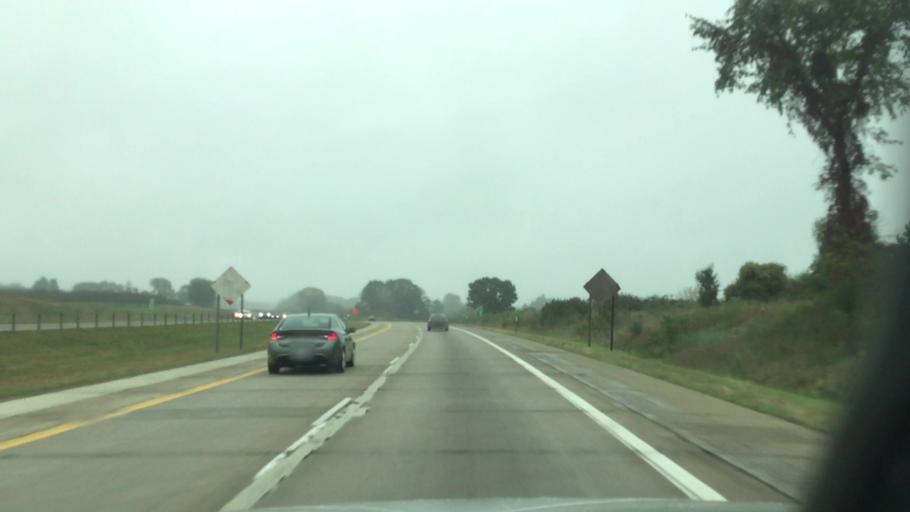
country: US
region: Michigan
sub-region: Van Buren County
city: Hartford
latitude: 42.1936
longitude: -86.1168
